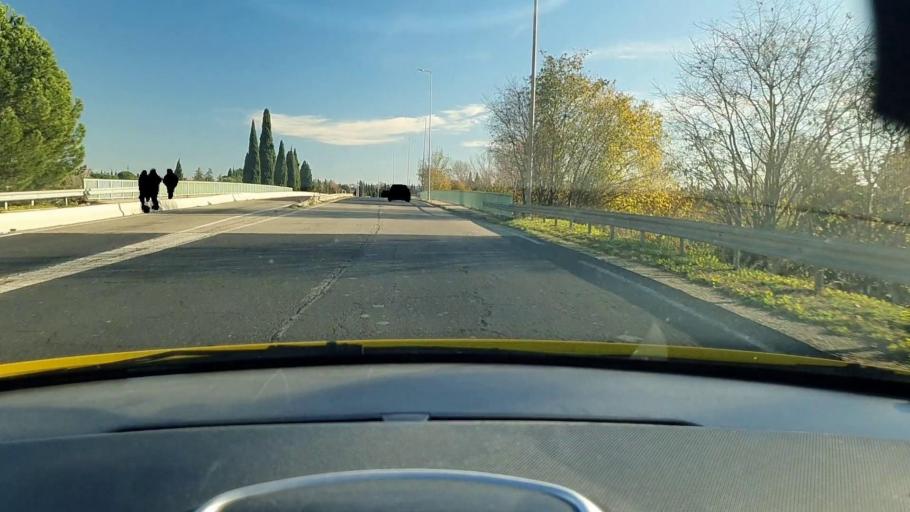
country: FR
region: Languedoc-Roussillon
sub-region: Departement du Gard
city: Caissargues
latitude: 43.8233
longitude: 4.3812
